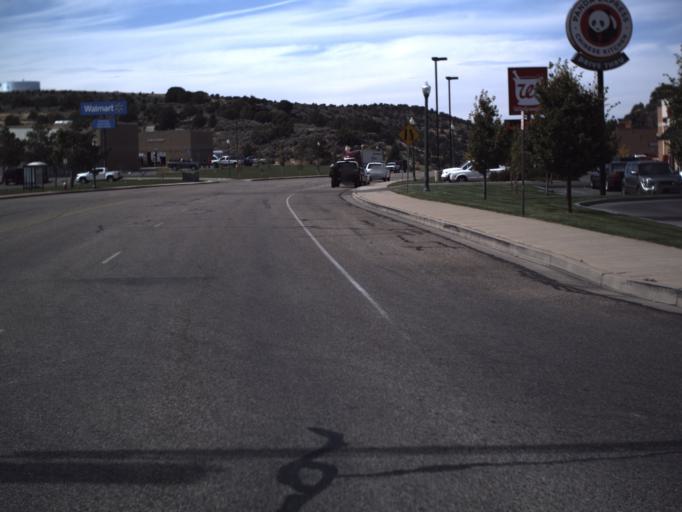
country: US
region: Utah
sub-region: Iron County
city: Cedar City
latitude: 37.6552
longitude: -113.0852
